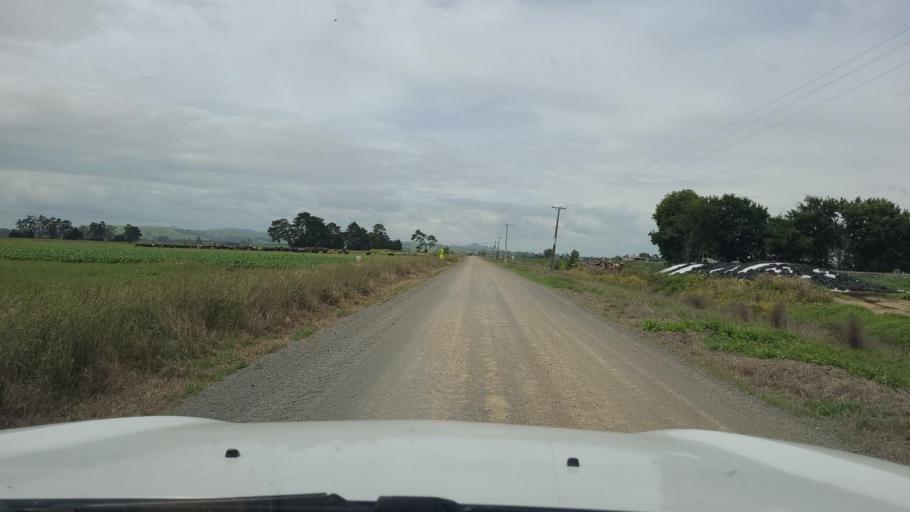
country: NZ
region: Waikato
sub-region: Hamilton City
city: Hamilton
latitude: -37.6618
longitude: 175.4375
